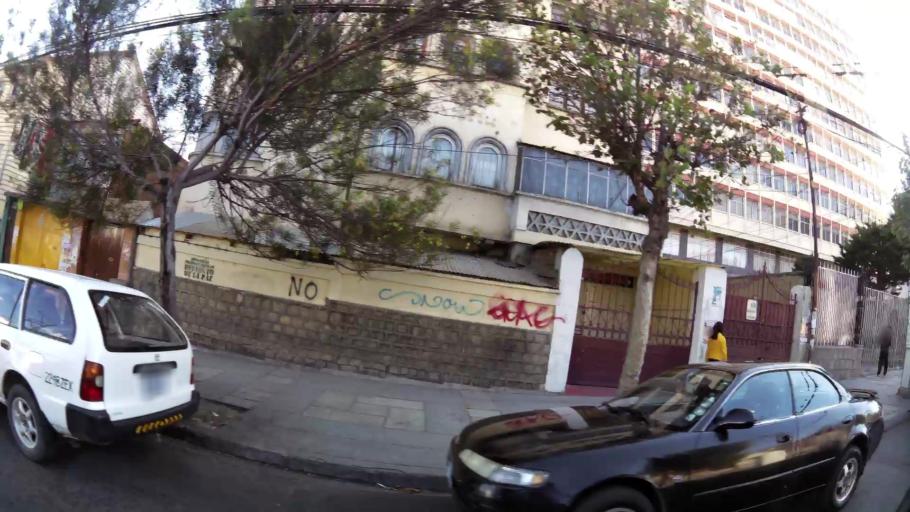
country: BO
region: La Paz
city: La Paz
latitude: -16.5086
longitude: -68.1195
